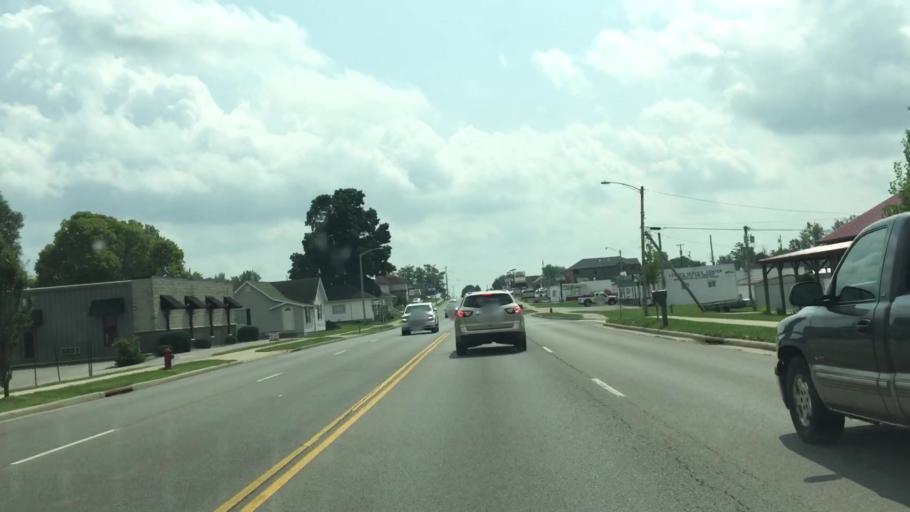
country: US
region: Ohio
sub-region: Logan County
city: Bellefontaine
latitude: 40.3434
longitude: -83.7616
